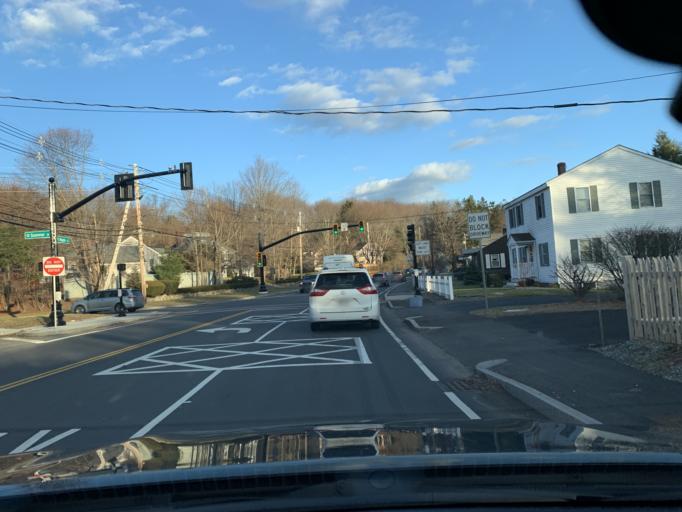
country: US
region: Massachusetts
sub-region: Essex County
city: Danvers
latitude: 42.5727
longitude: -70.9469
